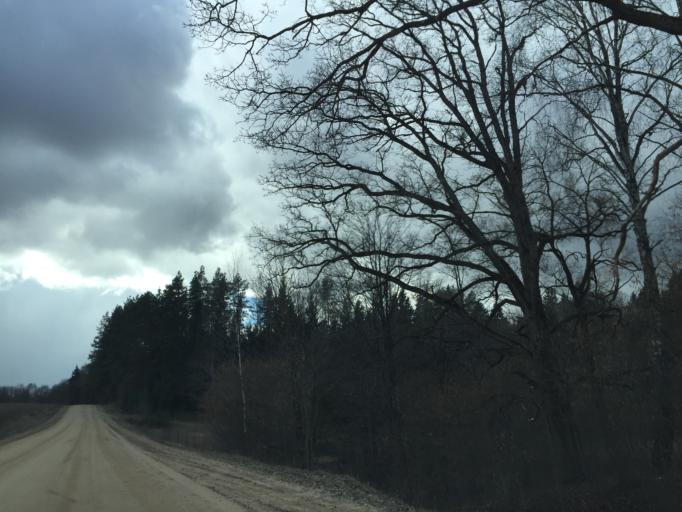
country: LV
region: Akniste
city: Akniste
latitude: 56.1098
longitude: 25.8300
